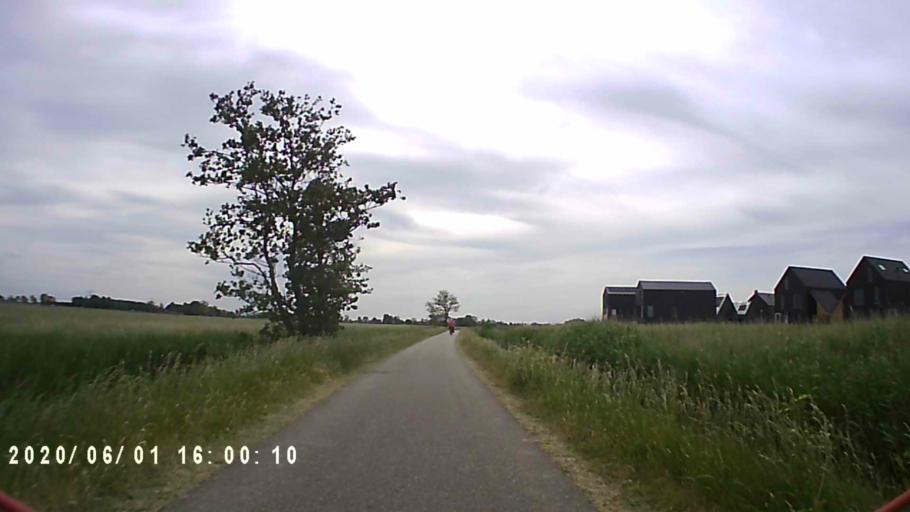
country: NL
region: Friesland
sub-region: Gemeente Leeuwarden
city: Goutum
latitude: 53.1720
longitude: 5.8212
